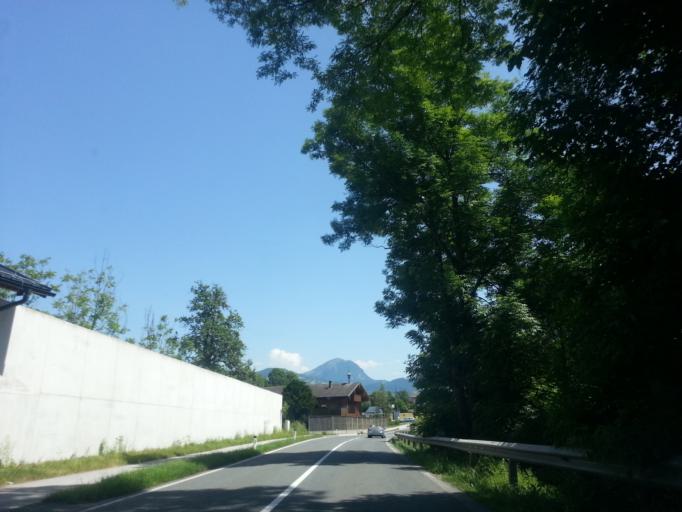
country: AT
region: Salzburg
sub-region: Politischer Bezirk Hallein
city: Kuchl
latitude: 47.6500
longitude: 13.1298
